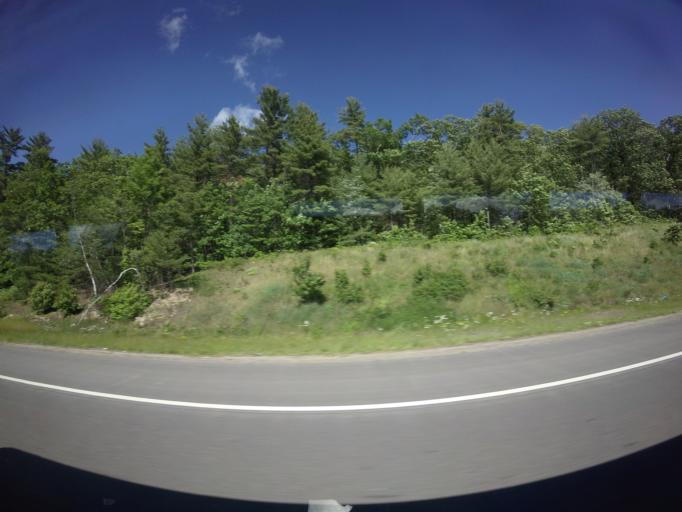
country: US
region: New Hampshire
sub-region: Rockingham County
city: Londonderry
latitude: 42.9245
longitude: -71.3766
